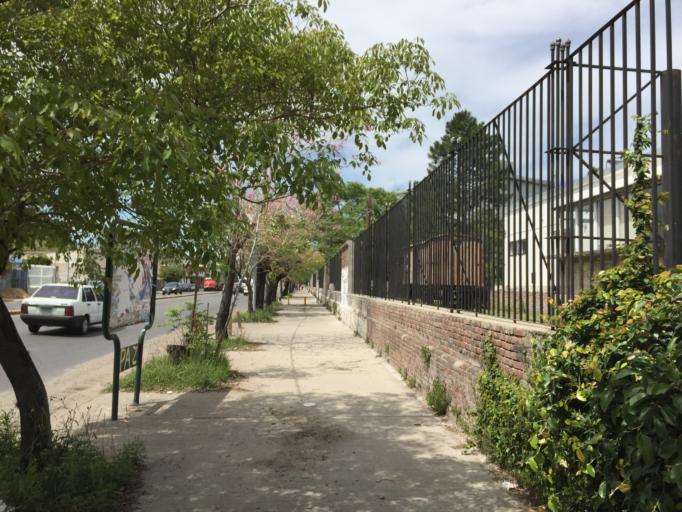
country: AR
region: Buenos Aires
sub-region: Partido de Lanus
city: Lanus
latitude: -34.7330
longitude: -58.3903
